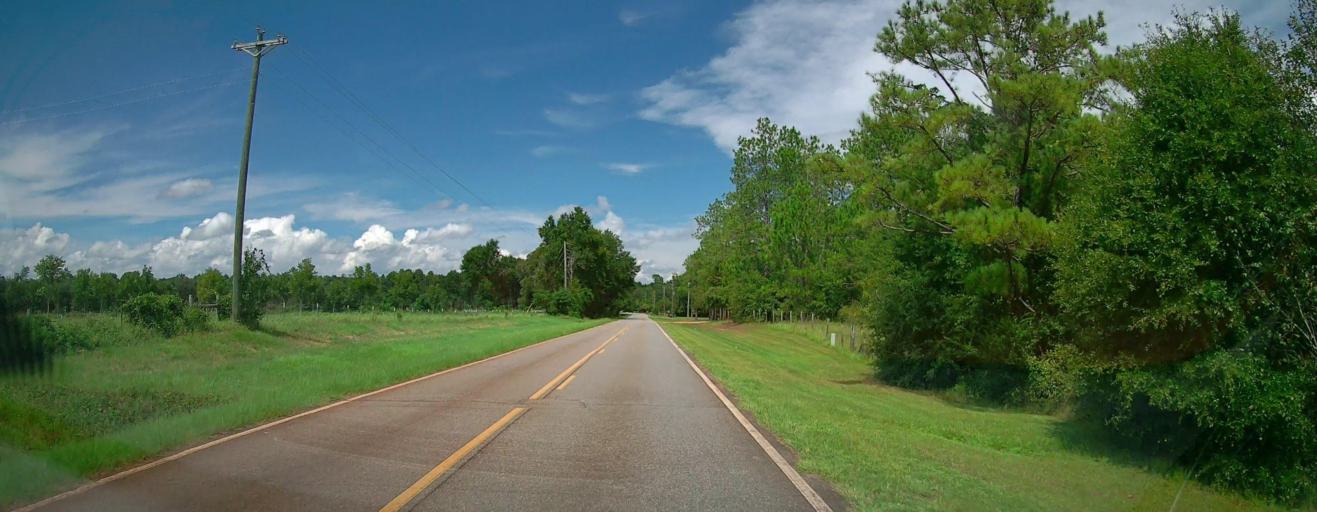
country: US
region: Georgia
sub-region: Houston County
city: Perry
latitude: 32.5161
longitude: -83.7465
